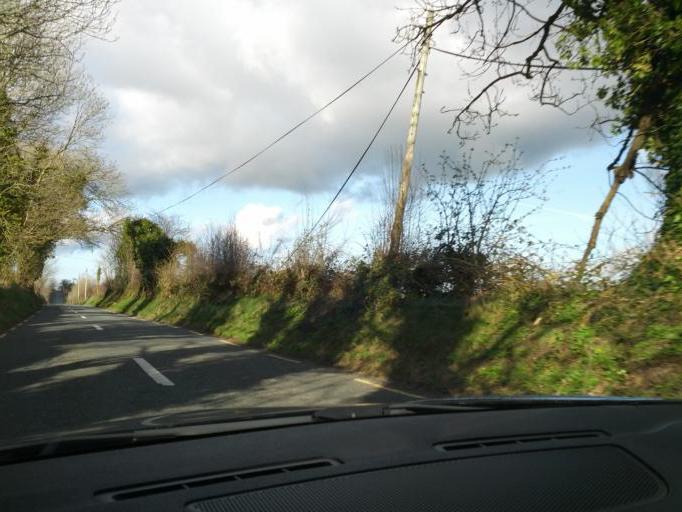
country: IE
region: Connaught
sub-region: Roscommon
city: Castlerea
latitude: 53.6766
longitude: -8.4918
